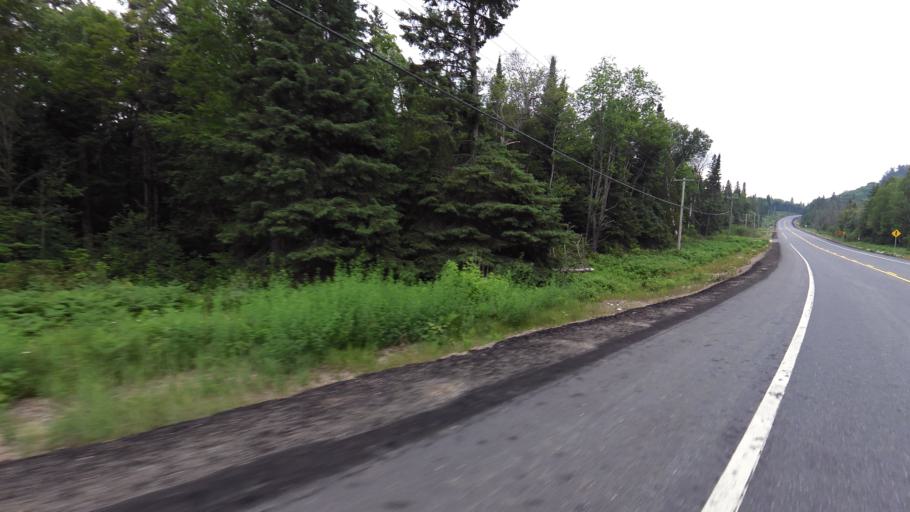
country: CA
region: Ontario
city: Huntsville
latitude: 45.4902
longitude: -78.7495
